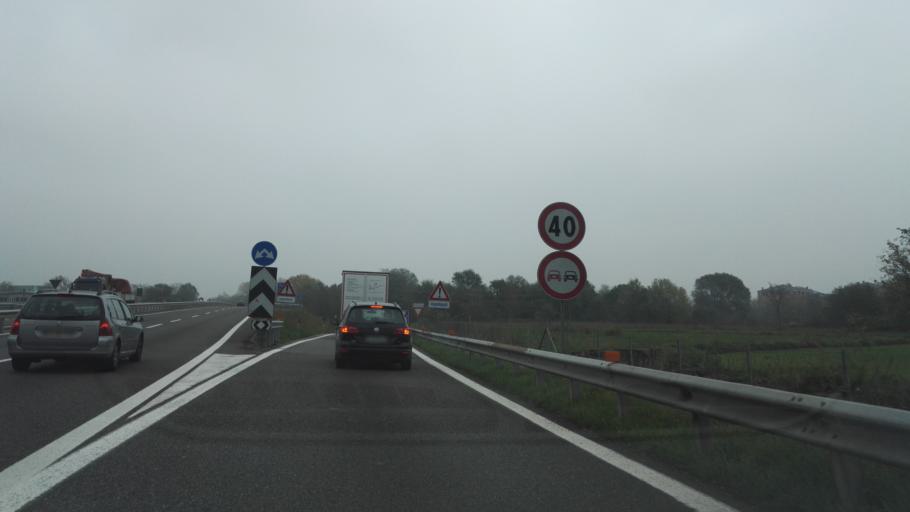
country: IT
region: Lombardy
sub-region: Citta metropolitana di Milano
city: Figino
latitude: 45.4978
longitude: 9.0721
